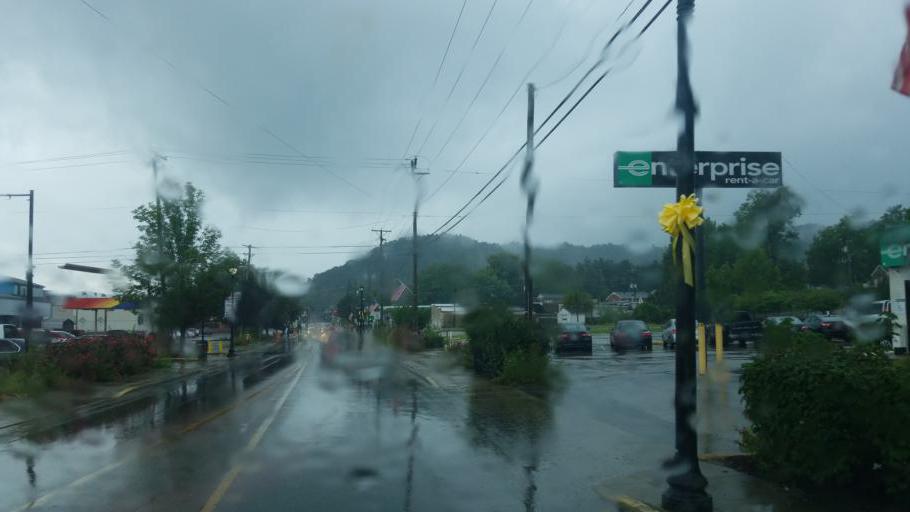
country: US
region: Kentucky
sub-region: Rowan County
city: Morehead
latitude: 38.1797
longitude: -83.4370
